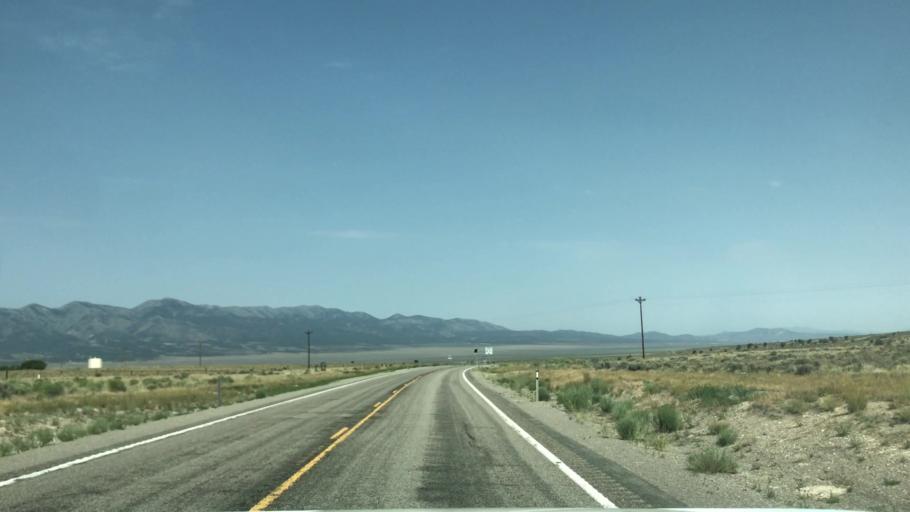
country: US
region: Nevada
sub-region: White Pine County
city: Ely
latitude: 39.0394
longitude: -114.7136
